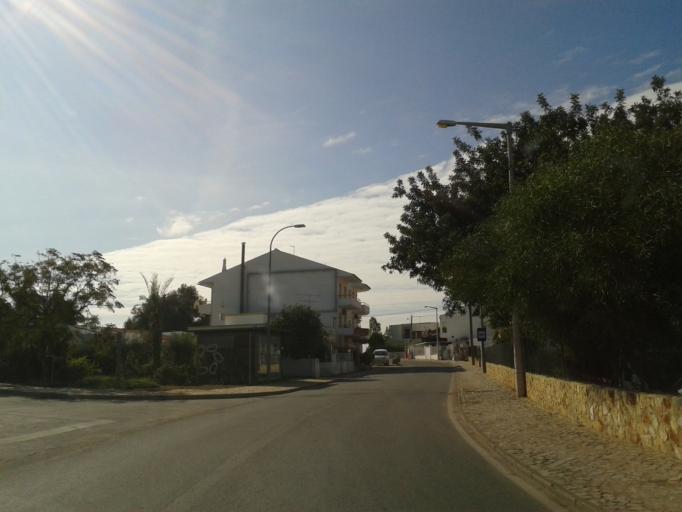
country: PT
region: Faro
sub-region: Loule
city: Almancil
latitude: 37.0879
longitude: -8.0373
